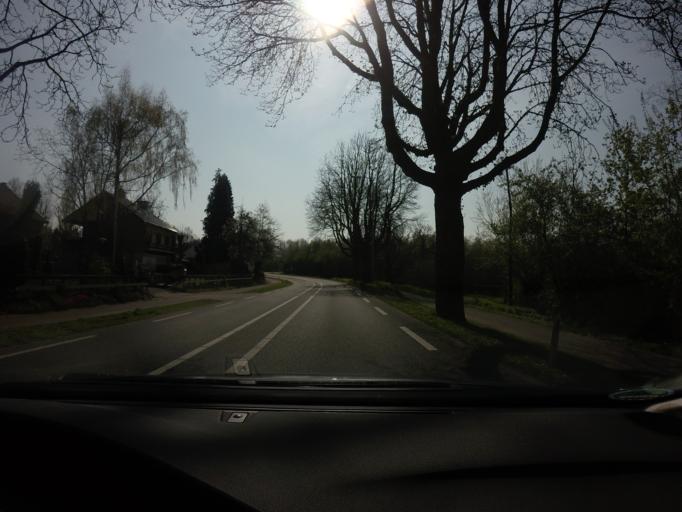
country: NL
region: Limburg
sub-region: Valkenburg aan de Geul
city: Berg
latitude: 50.8786
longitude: 5.7706
